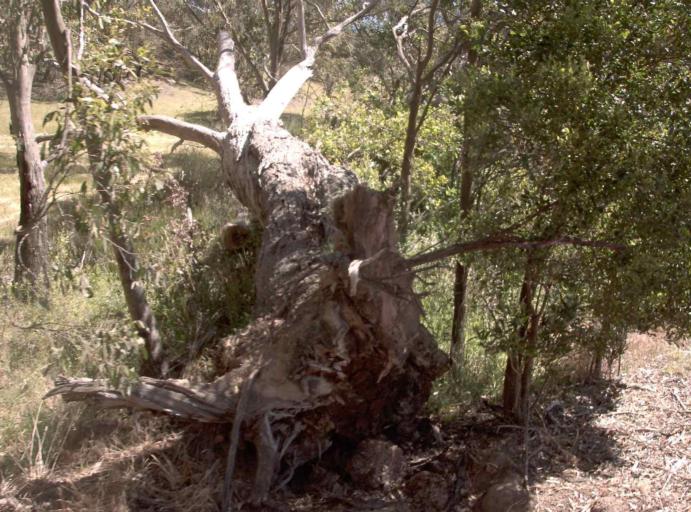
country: AU
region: New South Wales
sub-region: Bombala
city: Bombala
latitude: -37.0494
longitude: 148.8104
